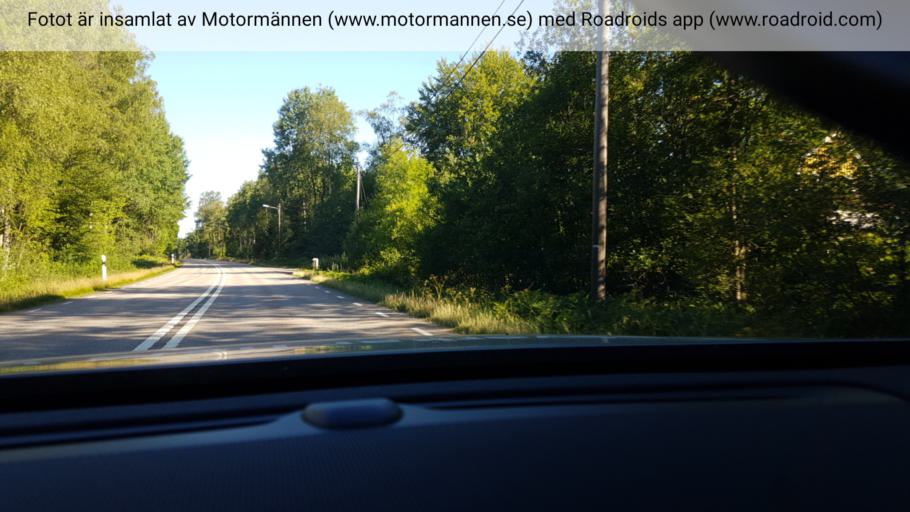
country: SE
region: Kronoberg
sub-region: Markaryds Kommun
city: Markaryd
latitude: 56.4057
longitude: 13.6448
